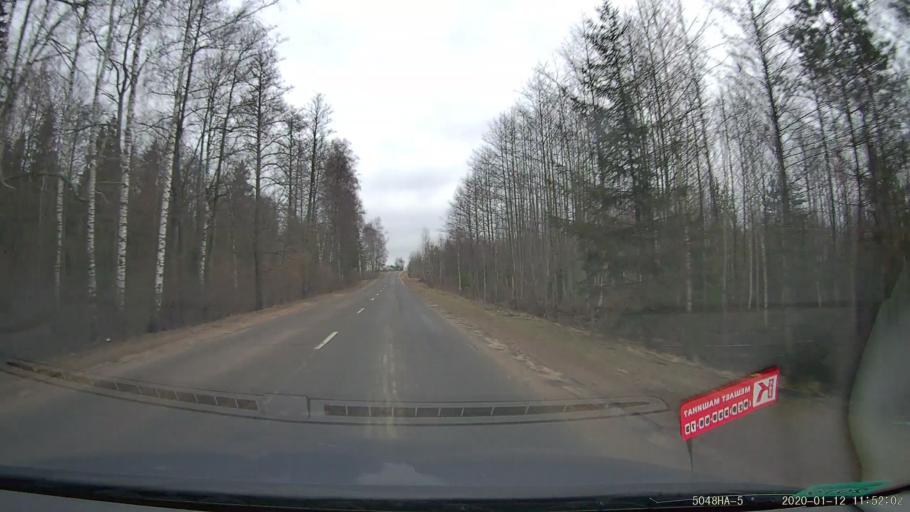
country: BY
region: Minsk
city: Rakaw
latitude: 53.9644
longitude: 27.1213
